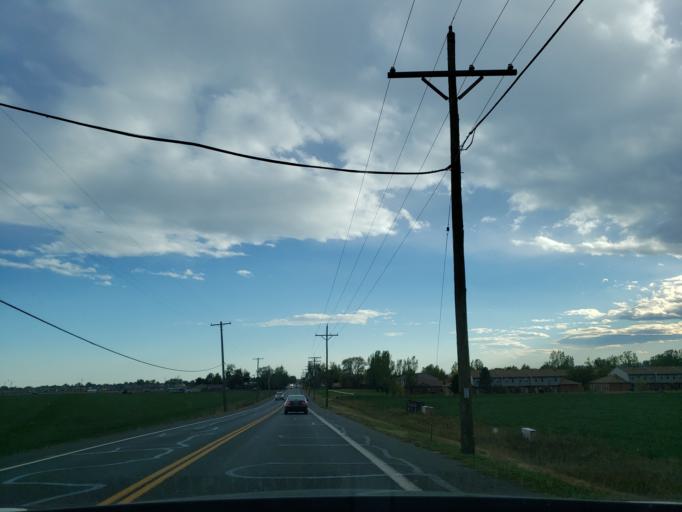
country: US
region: Colorado
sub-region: Larimer County
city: Fort Collins
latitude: 40.6002
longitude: -105.0294
